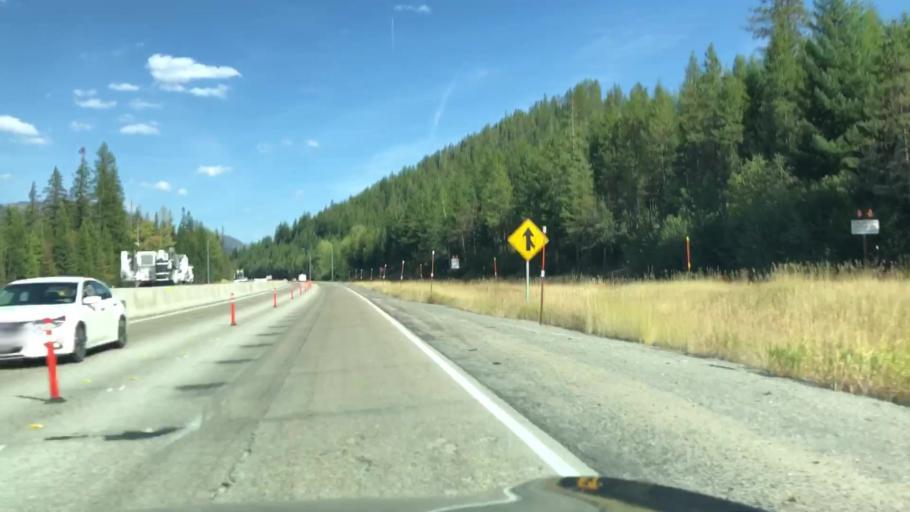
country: US
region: Idaho
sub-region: Shoshone County
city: Wallace
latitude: 47.4680
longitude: -115.7825
